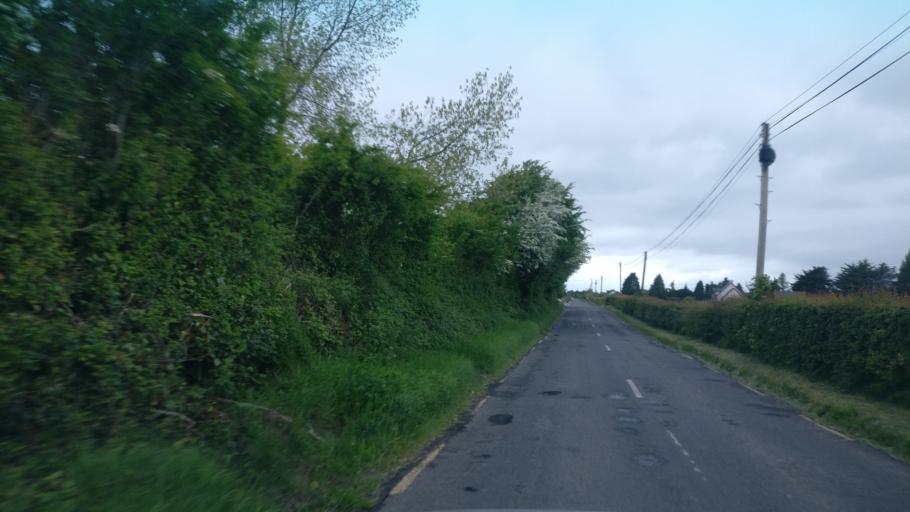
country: IE
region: Connaught
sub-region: County Galway
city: Portumna
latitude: 53.1059
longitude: -8.2607
